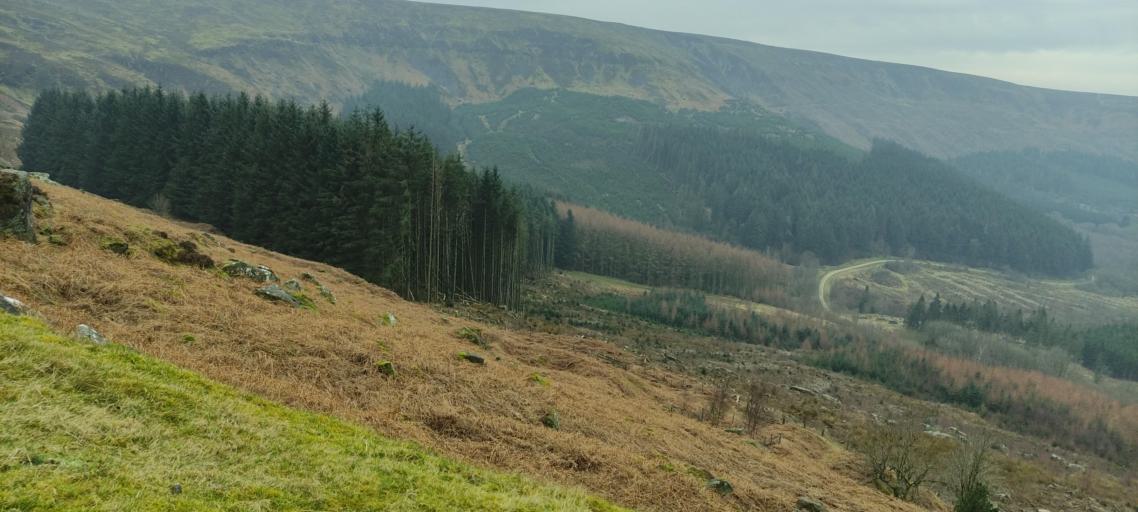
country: GB
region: England
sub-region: North Yorkshire
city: Ingleby Greenhow
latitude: 54.4180
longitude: -1.0685
